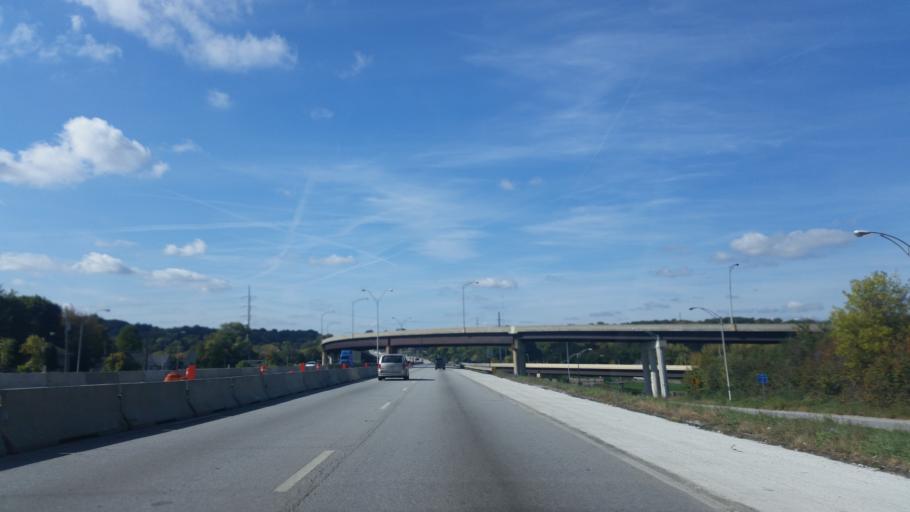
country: US
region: Ohio
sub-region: Summit County
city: Akron
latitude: 41.0622
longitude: -81.5368
